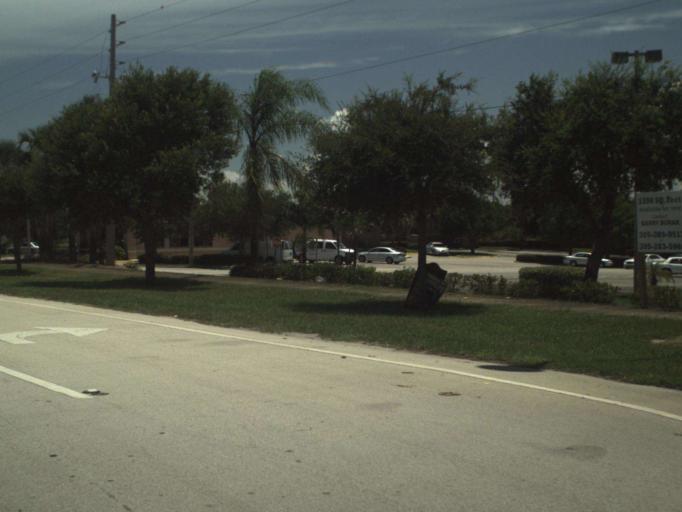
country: US
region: Florida
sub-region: Saint Lucie County
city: Fort Pierce
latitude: 27.4695
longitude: -80.3337
